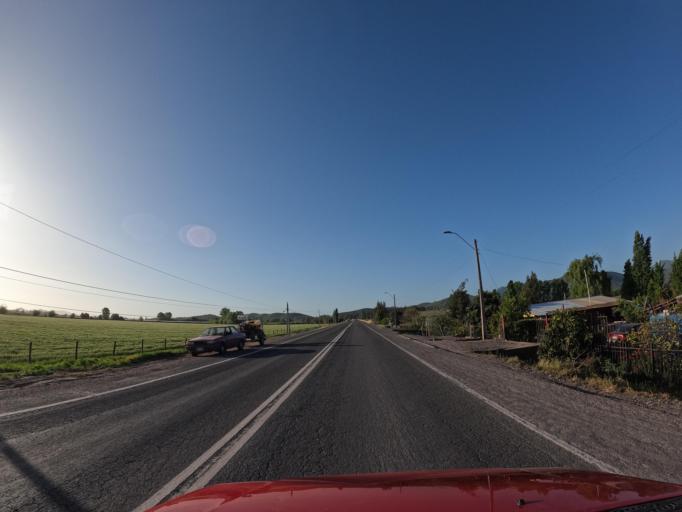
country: CL
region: O'Higgins
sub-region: Provincia de Colchagua
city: Santa Cruz
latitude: -34.4429
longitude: -71.3673
